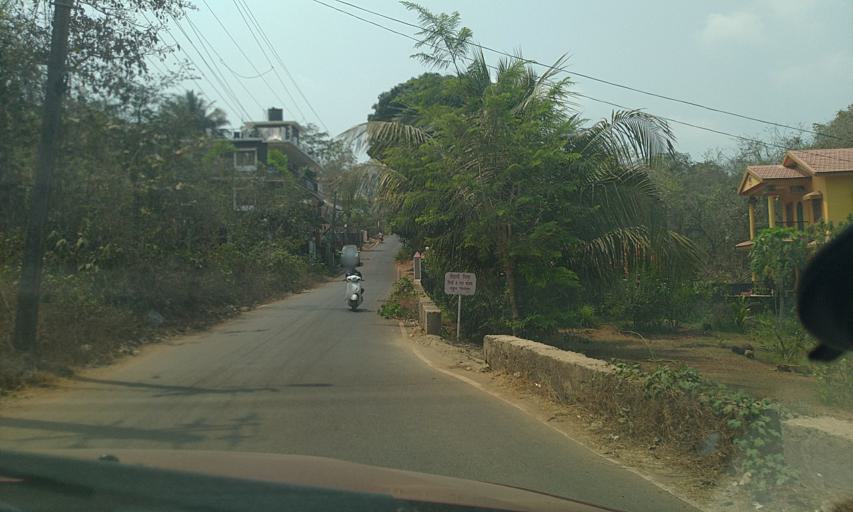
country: IN
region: Goa
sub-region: North Goa
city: Serula
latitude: 15.5246
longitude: 73.8388
